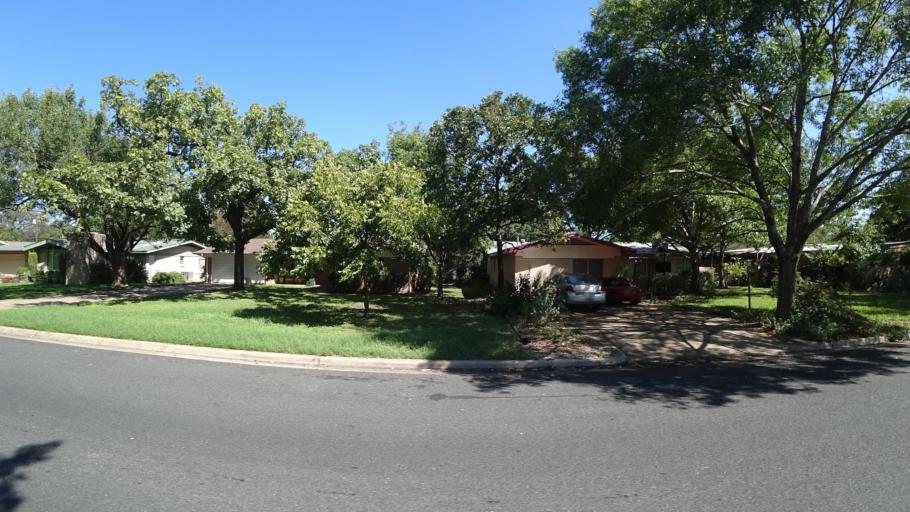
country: US
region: Texas
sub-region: Travis County
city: Austin
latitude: 30.3072
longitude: -97.6953
